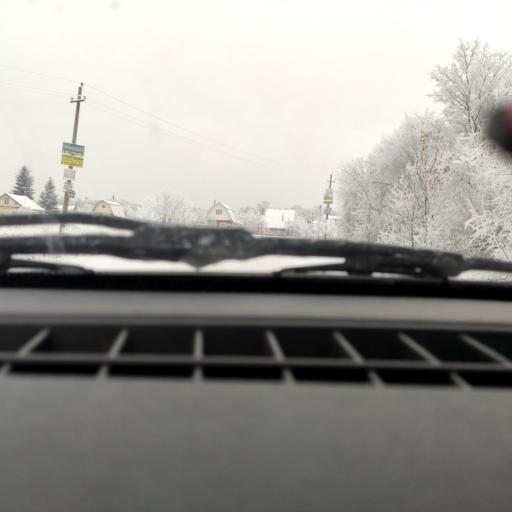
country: RU
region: Bashkortostan
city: Ufa
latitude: 54.7064
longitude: 56.1299
